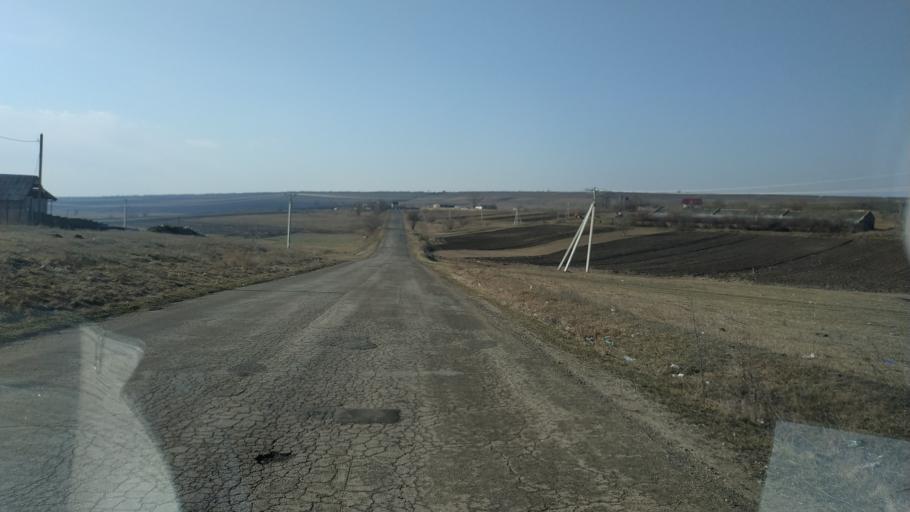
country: MD
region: Chisinau
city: Singera
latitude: 46.8047
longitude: 29.0327
